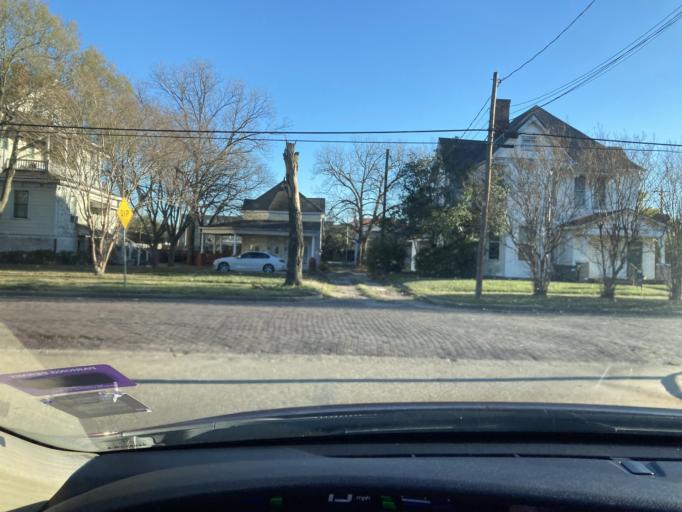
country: US
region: Texas
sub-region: Navarro County
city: Corsicana
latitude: 32.0932
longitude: -96.4700
